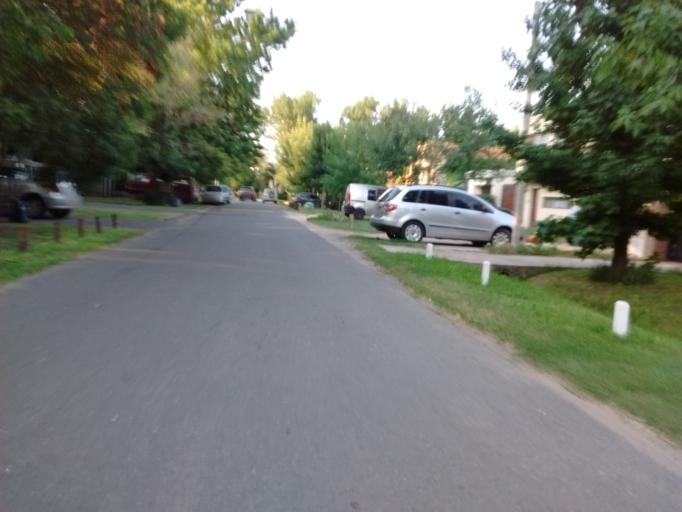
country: AR
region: Santa Fe
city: Funes
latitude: -32.9225
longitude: -60.7552
